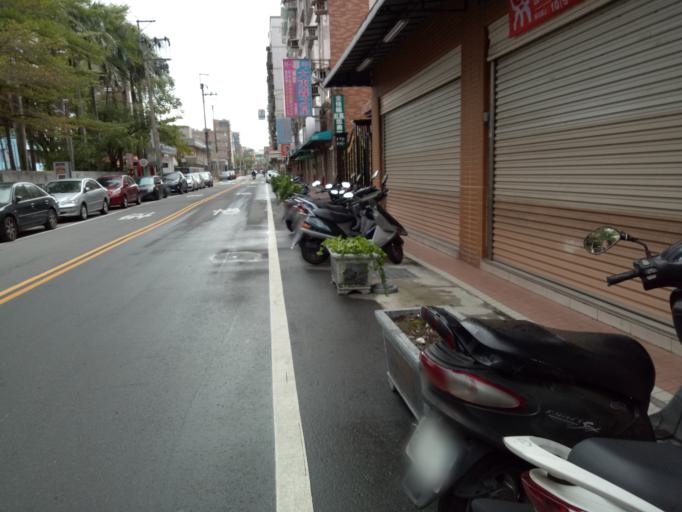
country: TW
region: Taiwan
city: Taoyuan City
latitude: 24.9688
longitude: 121.3034
